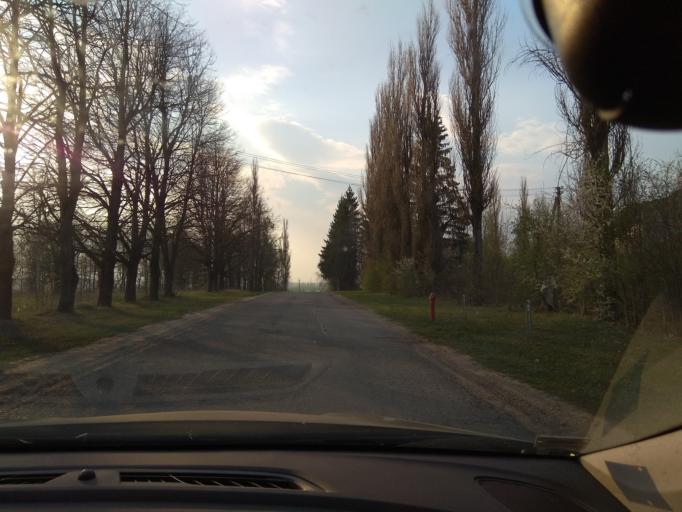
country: LT
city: Baltoji Voke
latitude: 54.5987
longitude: 25.1424
